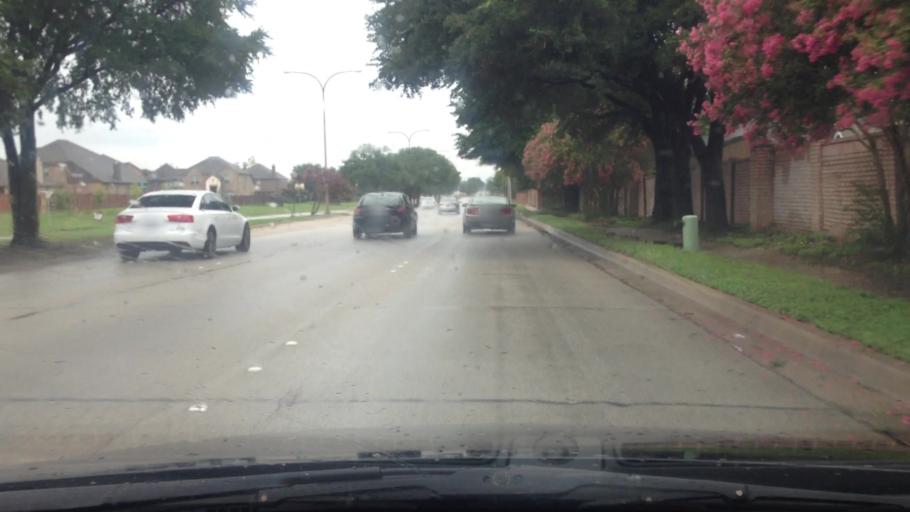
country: US
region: Texas
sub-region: Tarrant County
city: Watauga
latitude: 32.8504
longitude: -97.2899
